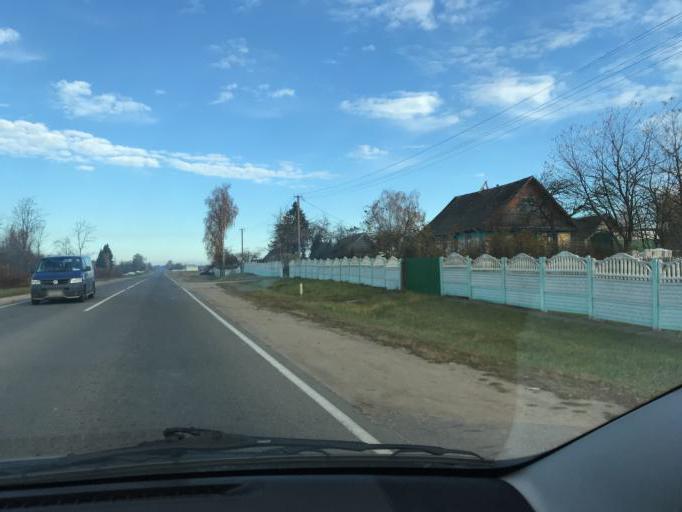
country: BY
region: Vitebsk
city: Haradok
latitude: 55.4783
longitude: 29.9688
